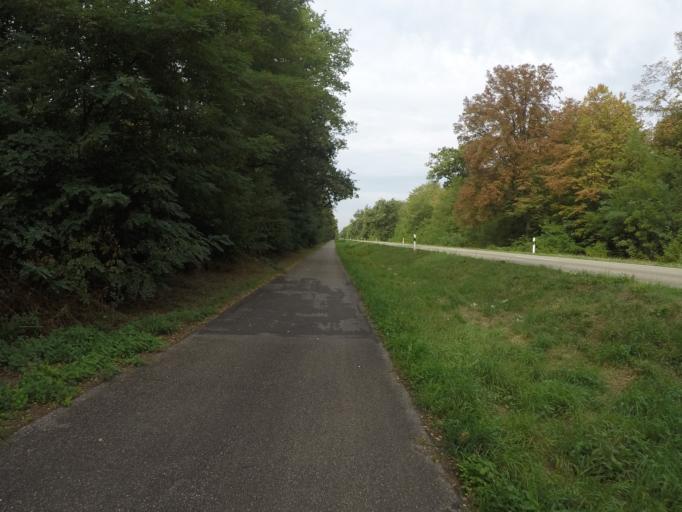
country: DE
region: Rheinland-Pfalz
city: Hanhofen
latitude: 49.3545
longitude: 8.3381
